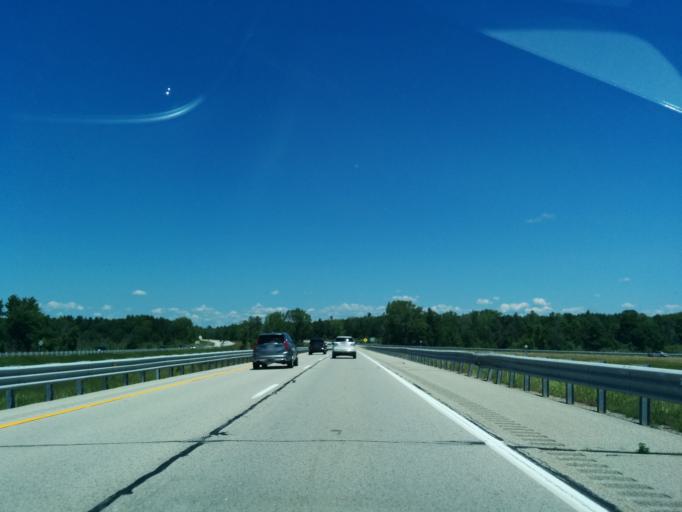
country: US
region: Michigan
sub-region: Arenac County
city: Standish
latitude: 43.9834
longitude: -84.0161
